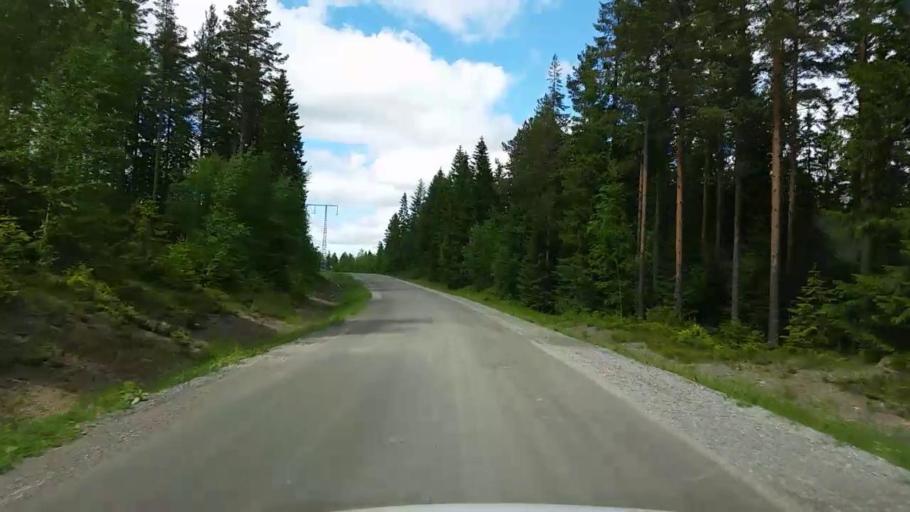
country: SE
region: Gaevleborg
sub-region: Bollnas Kommun
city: Vittsjo
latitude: 61.1754
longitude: 16.1507
